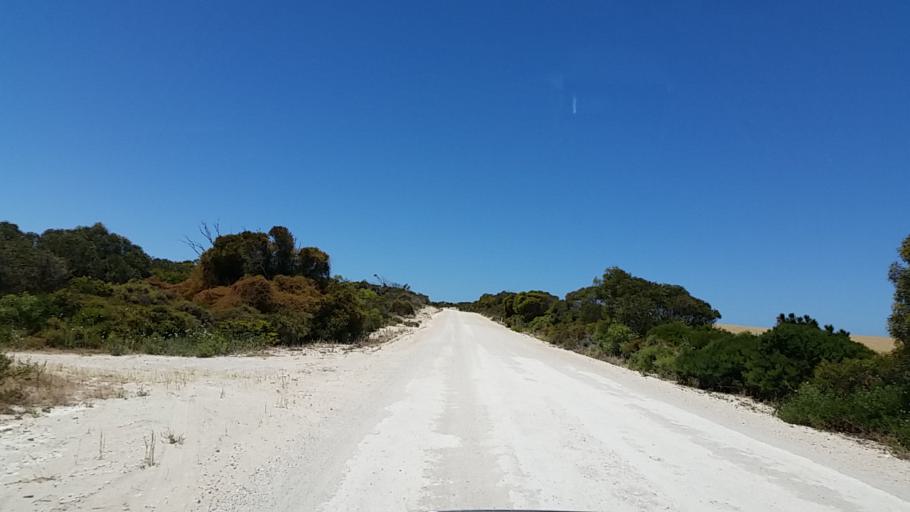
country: AU
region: South Australia
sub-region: Yorke Peninsula
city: Honiton
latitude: -35.2320
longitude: 137.1505
